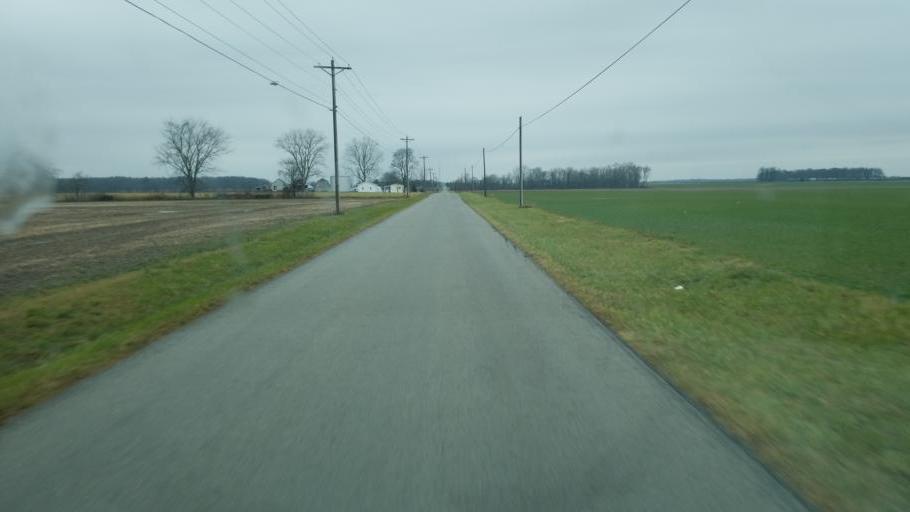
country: US
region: Ohio
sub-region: Delaware County
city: Ashley
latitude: 40.4228
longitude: -82.9258
